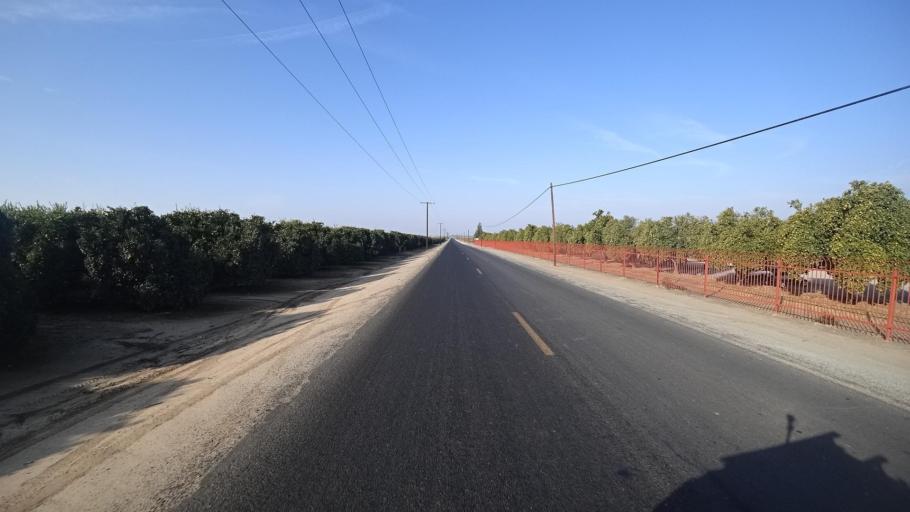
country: US
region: California
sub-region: Kern County
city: McFarland
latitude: 35.6746
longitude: -119.1720
